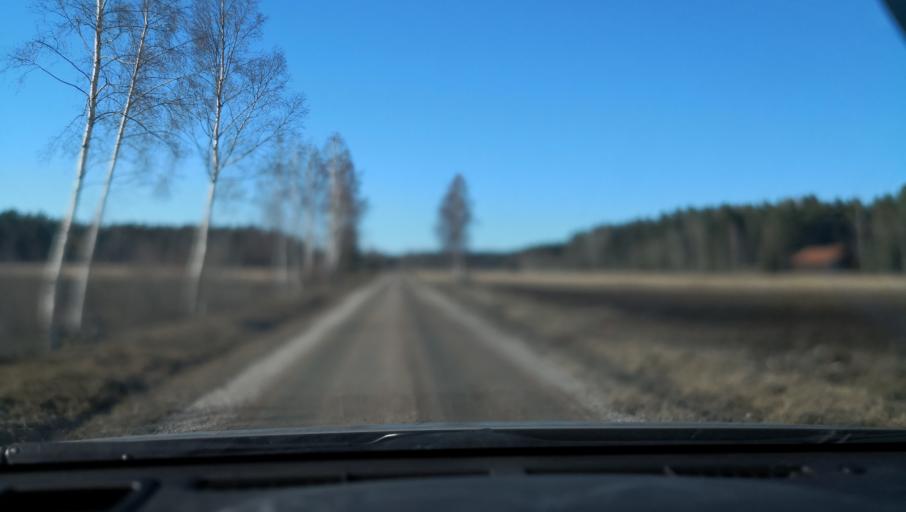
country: SE
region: Vaestmanland
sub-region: Sala Kommun
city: Sala
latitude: 60.1253
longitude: 16.6559
